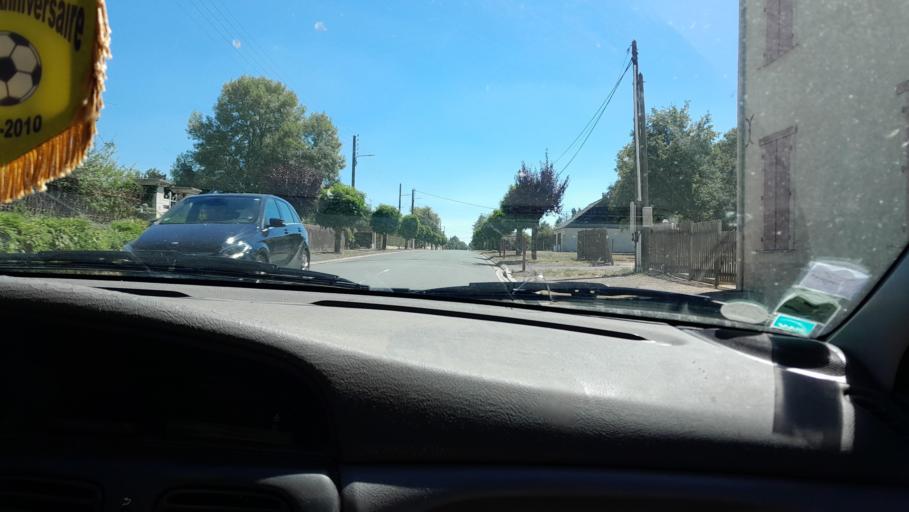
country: FR
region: Pays de la Loire
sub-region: Departement de la Loire-Atlantique
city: Saint-Mars-la-Jaille
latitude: 47.6217
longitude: -1.1980
